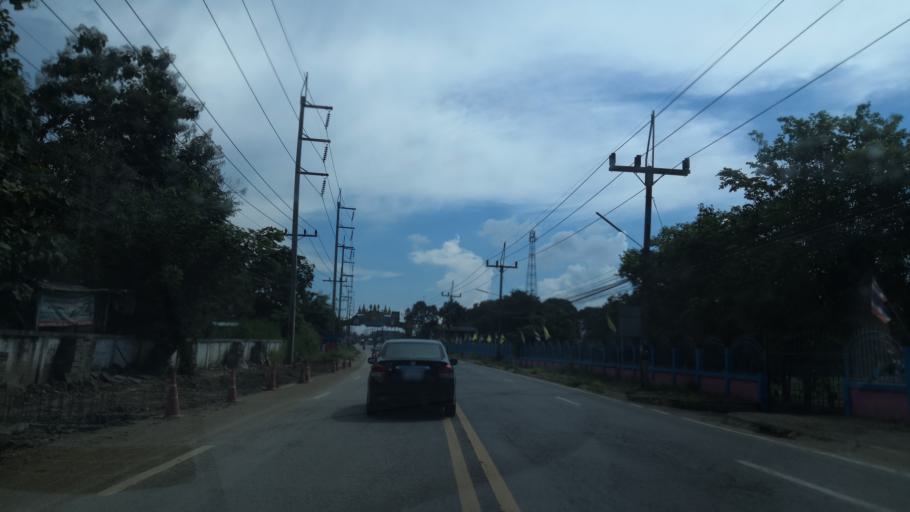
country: TH
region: Chiang Rai
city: Wiang Pa Pao
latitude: 19.3743
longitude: 99.5025
